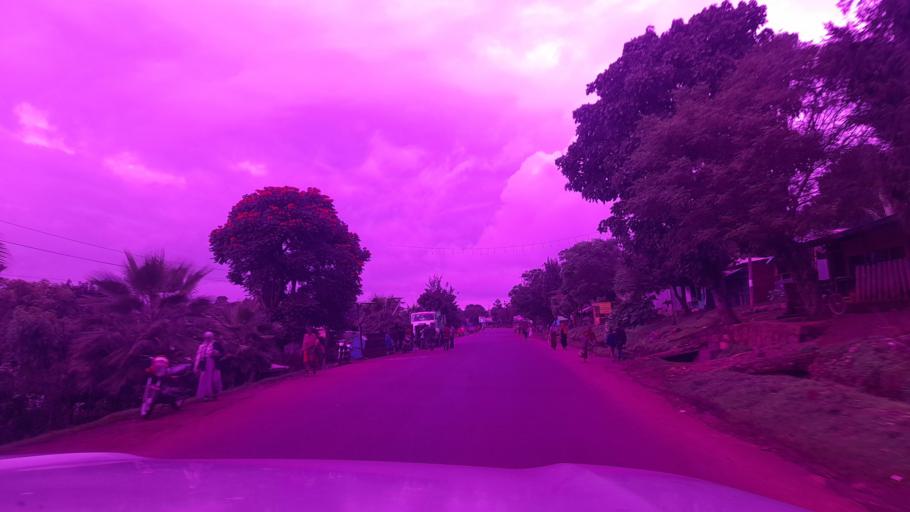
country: ET
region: Oromiya
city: Jima
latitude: 7.9657
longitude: 37.4404
